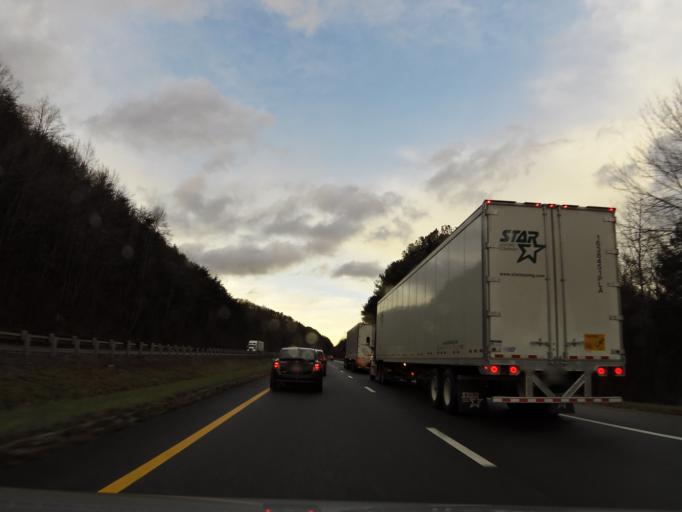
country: US
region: Tennessee
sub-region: Campbell County
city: Caryville
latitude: 36.3233
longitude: -84.2259
